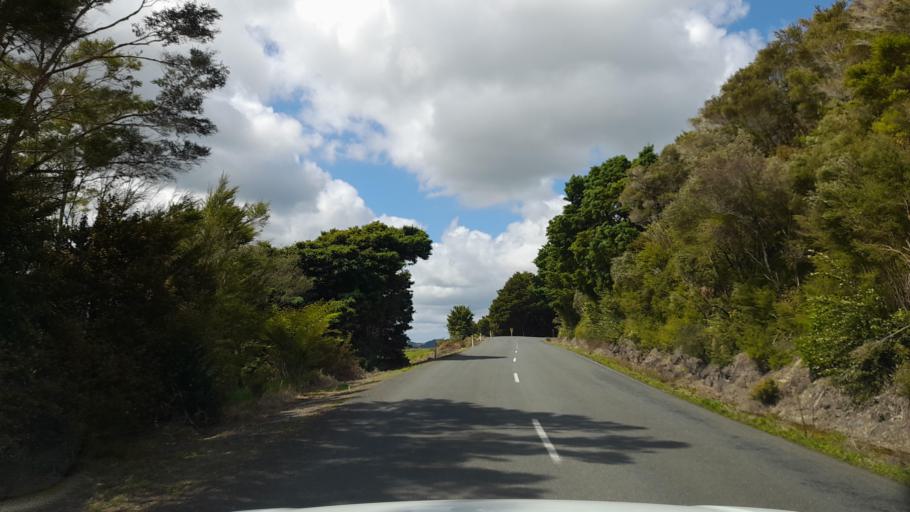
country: NZ
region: Northland
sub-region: Whangarei
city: Maungatapere
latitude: -35.6393
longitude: 174.0639
